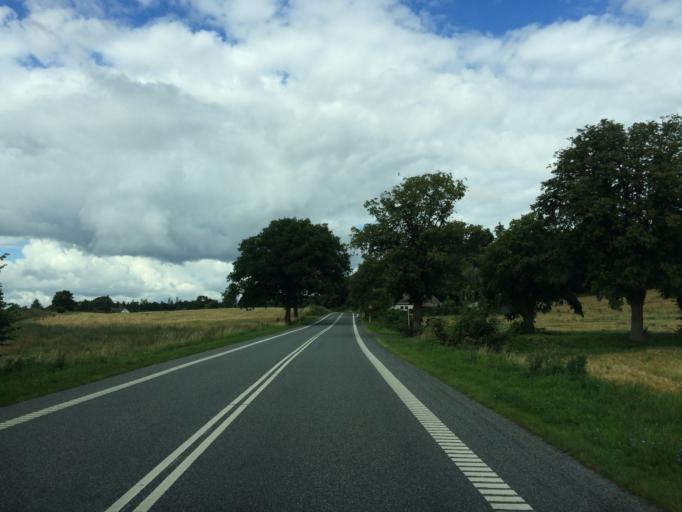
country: DK
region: South Denmark
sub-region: Assens Kommune
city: Harby
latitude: 55.1776
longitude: 10.1521
